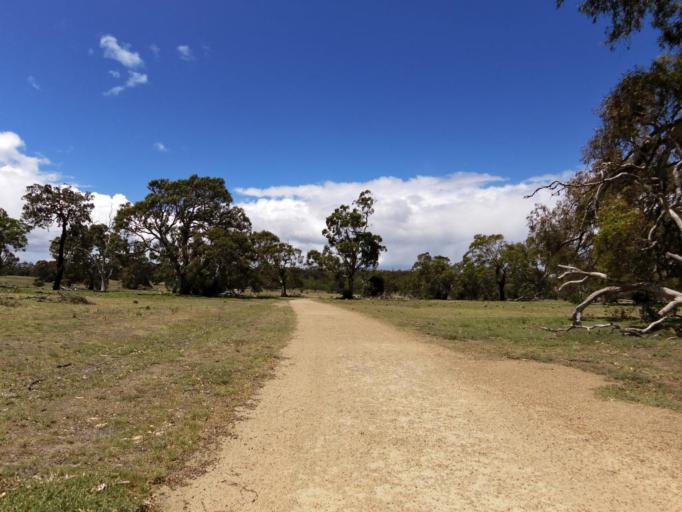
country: AU
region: Victoria
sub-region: Hume
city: Greenvale
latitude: -37.6408
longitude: 144.8448
